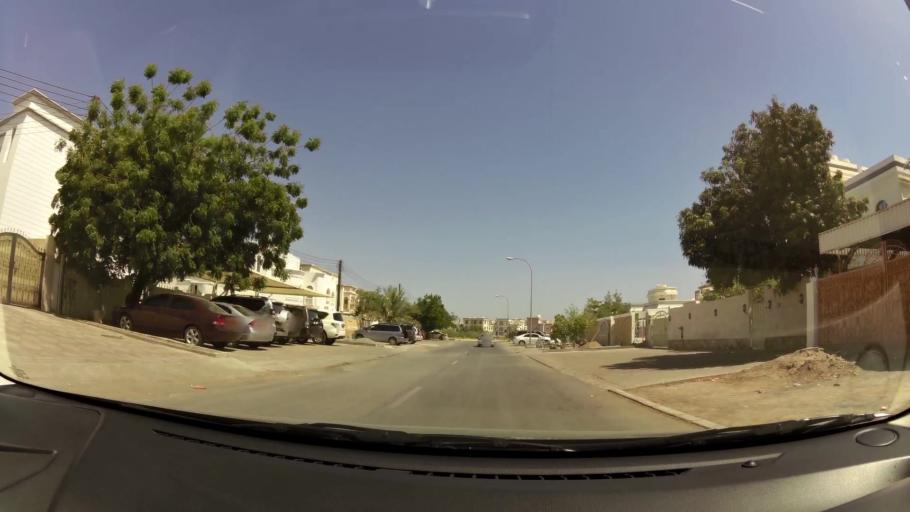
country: OM
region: Muhafazat Masqat
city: As Sib al Jadidah
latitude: 23.6152
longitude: 58.2492
